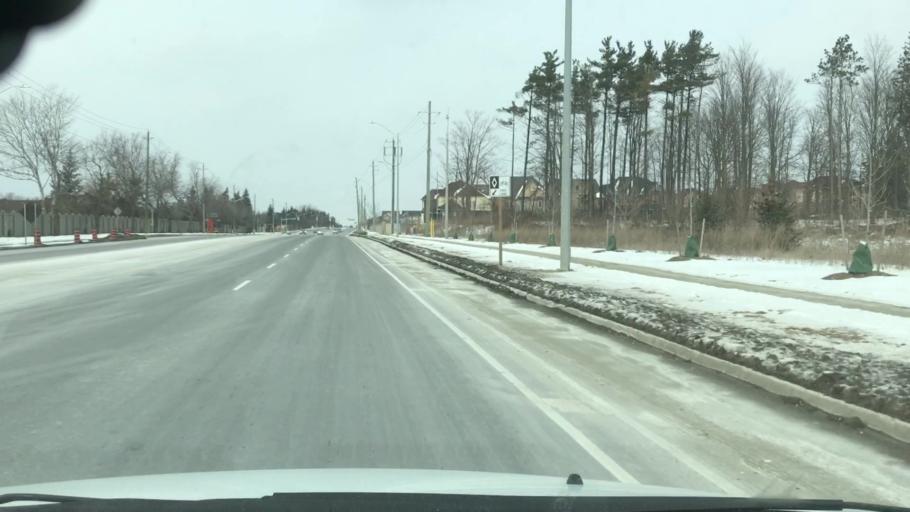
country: CA
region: Ontario
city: Newmarket
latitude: 44.0343
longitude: -79.4241
